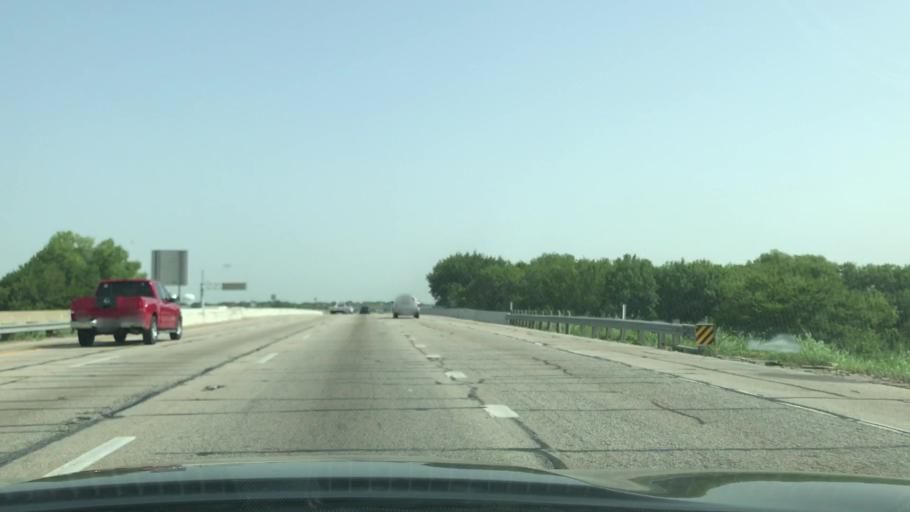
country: US
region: Texas
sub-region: Dallas County
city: Irving
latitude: 32.7925
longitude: -96.9200
